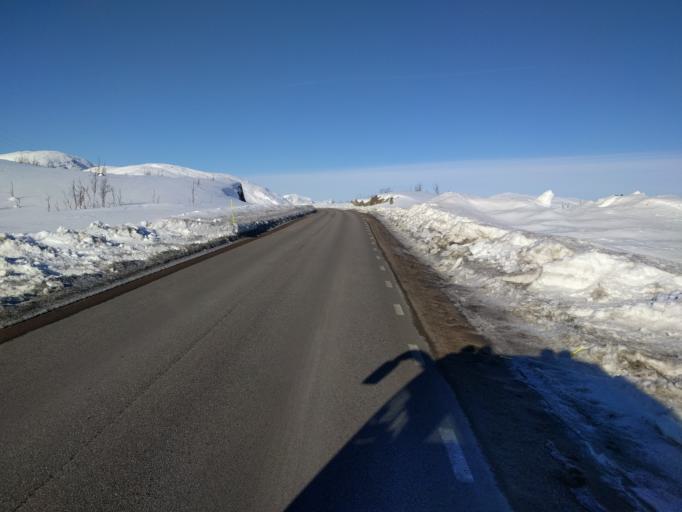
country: NO
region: Troms
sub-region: Bardu
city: Setermoen
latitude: 68.4316
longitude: 18.2227
